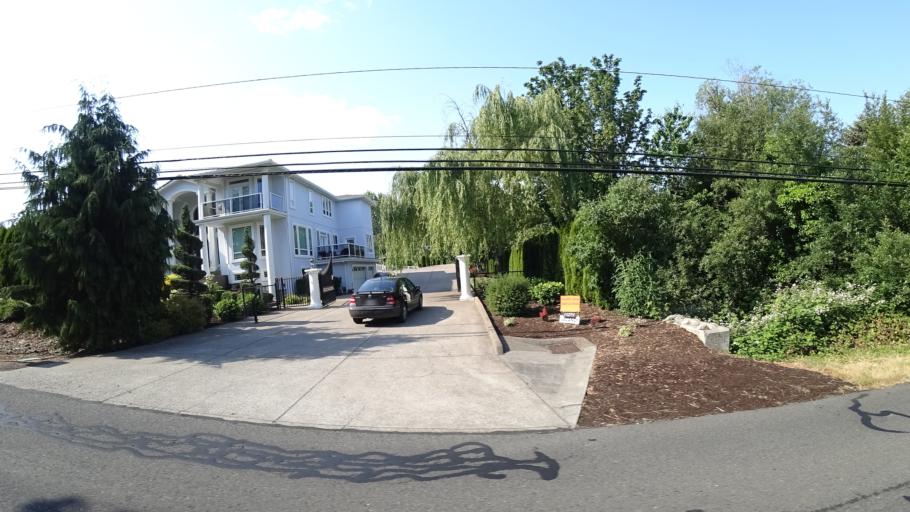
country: US
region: Oregon
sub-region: Clackamas County
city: Happy Valley
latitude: 45.4541
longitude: -122.5262
